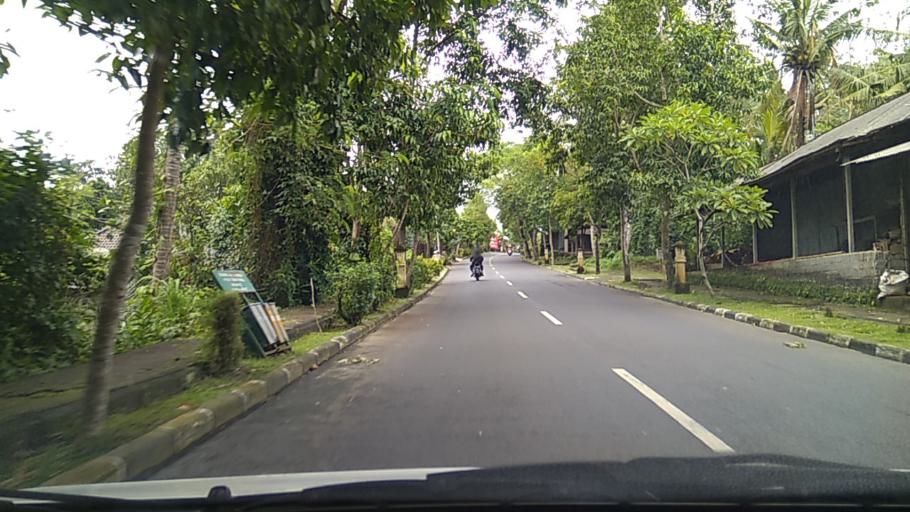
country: ID
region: Bali
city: Banjar Kelodan
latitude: -8.5225
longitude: 115.3460
